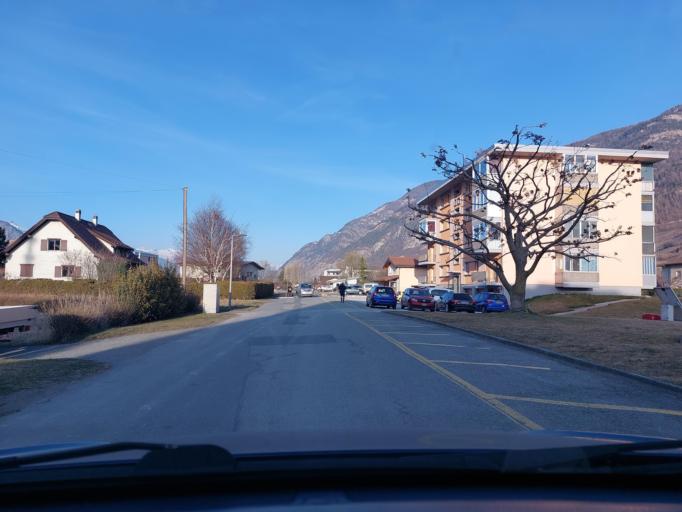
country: CH
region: Valais
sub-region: Martigny District
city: Saxon
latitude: 46.1531
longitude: 7.1847
